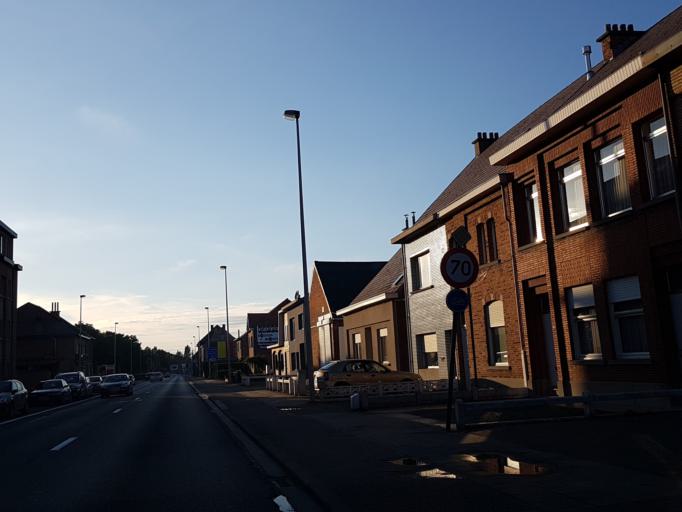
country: BE
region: Flanders
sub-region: Provincie Oost-Vlaanderen
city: Lebbeke
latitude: 51.0062
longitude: 4.1221
